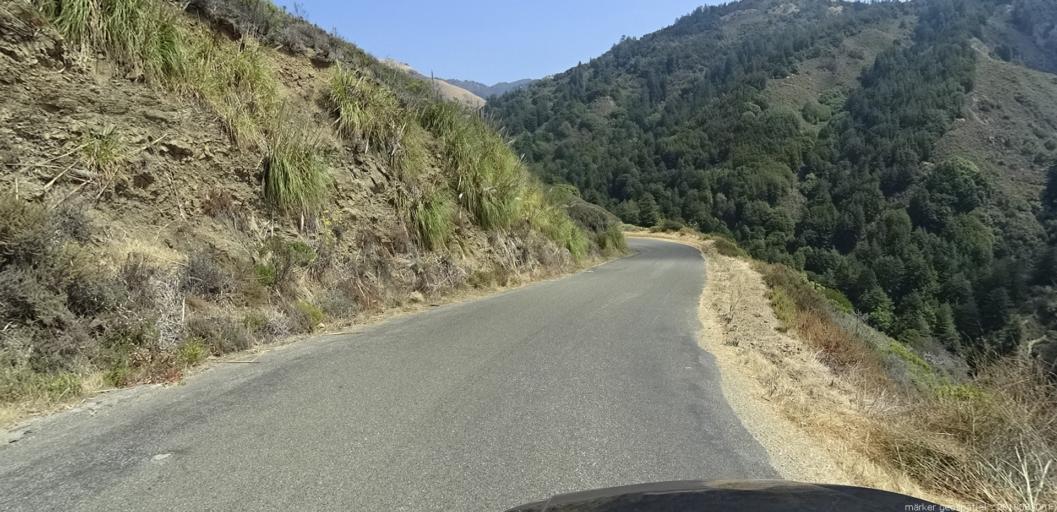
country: US
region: California
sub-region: Monterey County
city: Greenfield
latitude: 35.9867
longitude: -121.4887
